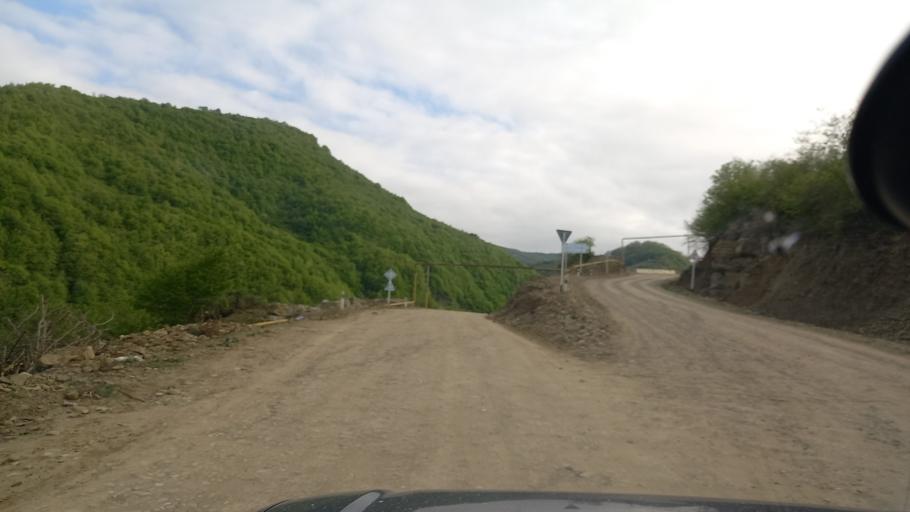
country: RU
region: Dagestan
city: Khuchni
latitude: 41.9671
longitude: 47.8743
